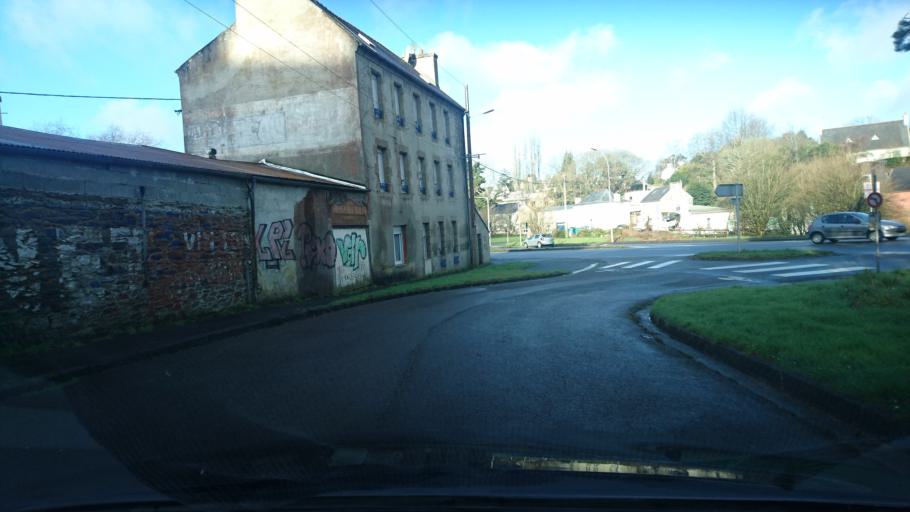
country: FR
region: Brittany
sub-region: Departement du Finistere
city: Bohars
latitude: 48.4101
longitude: -4.5208
